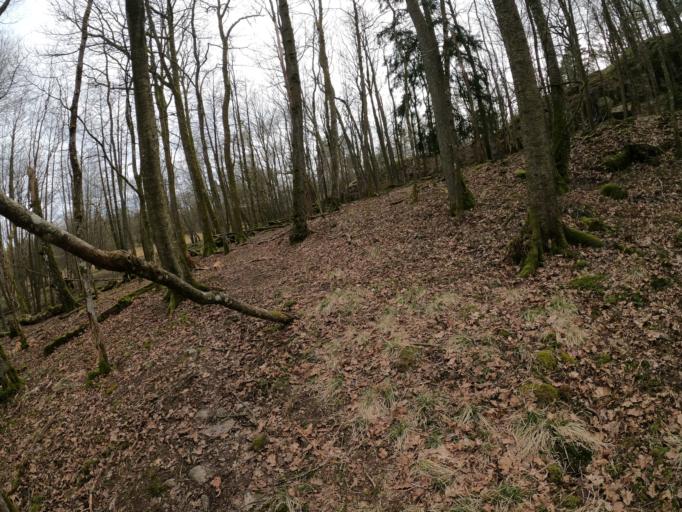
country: SE
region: Vaestra Goetaland
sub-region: Molndal
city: Kallered
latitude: 57.6296
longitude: 12.0828
